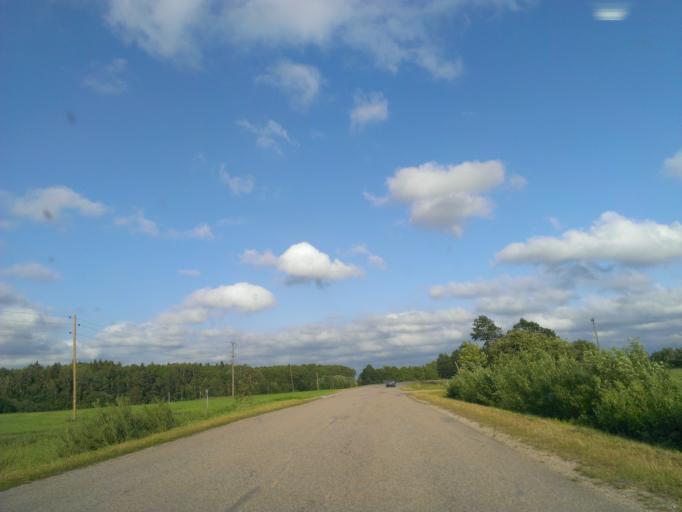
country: LV
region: Aizpute
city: Aizpute
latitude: 56.7553
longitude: 21.5561
